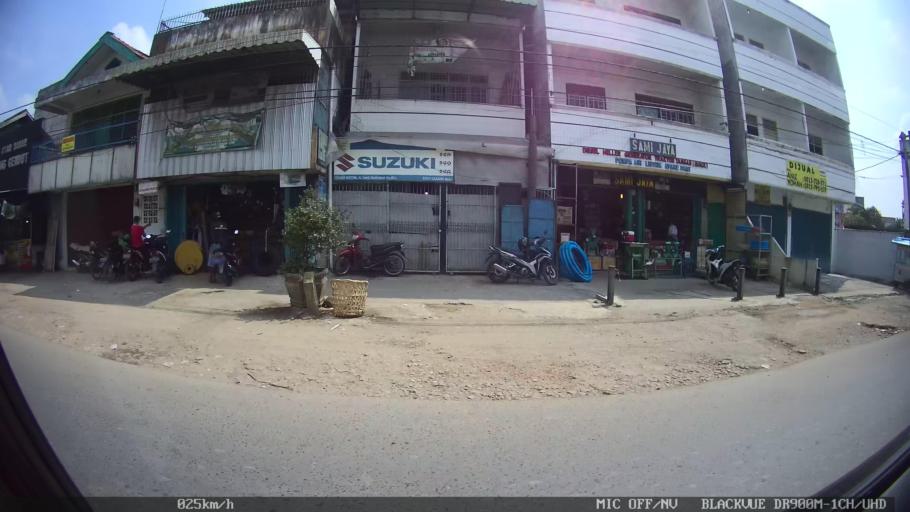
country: ID
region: Lampung
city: Pringsewu
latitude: -5.3560
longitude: 104.9760
